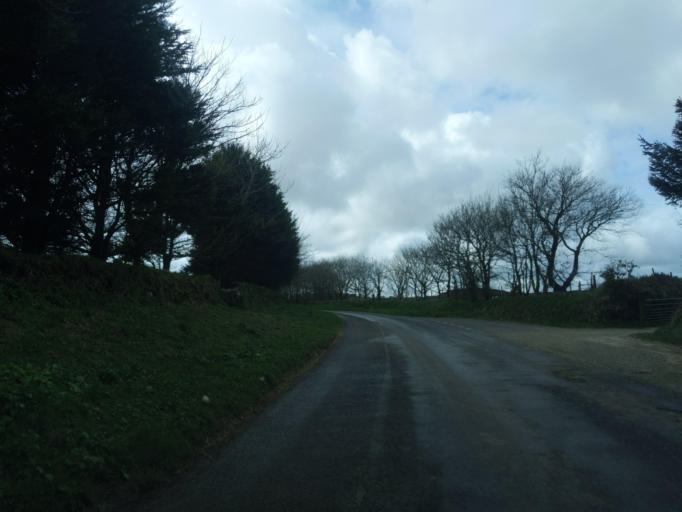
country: GB
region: England
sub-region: Cornwall
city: Camelford
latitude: 50.6250
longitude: -4.5794
